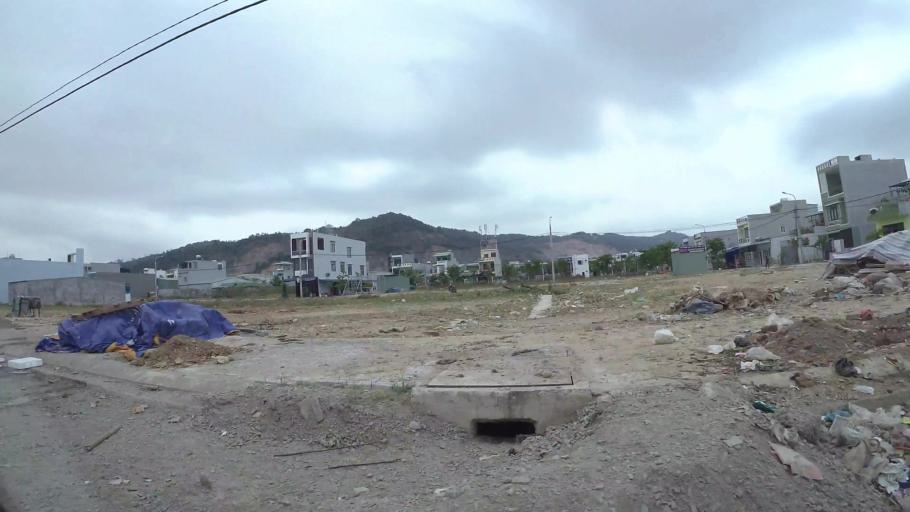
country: VN
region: Da Nang
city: Lien Chieu
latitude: 16.0480
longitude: 108.1676
